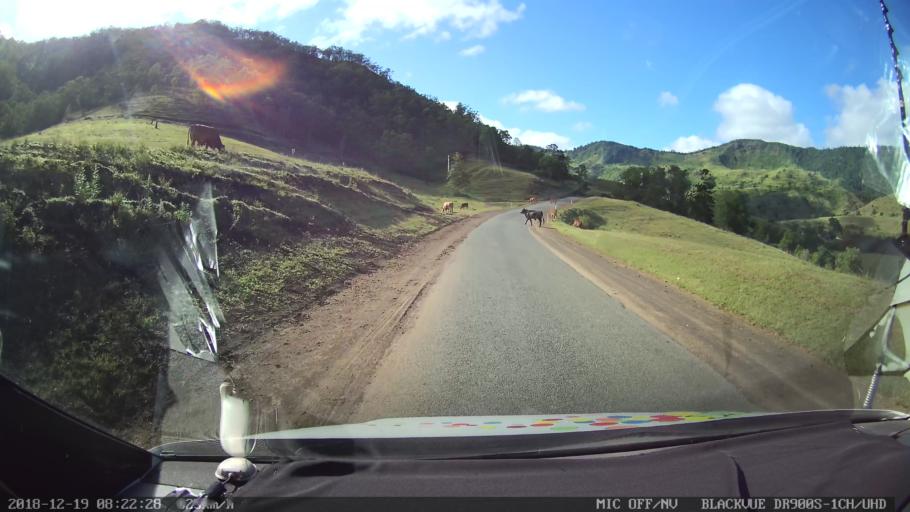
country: AU
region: New South Wales
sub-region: Kyogle
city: Kyogle
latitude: -28.3035
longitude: 152.9112
